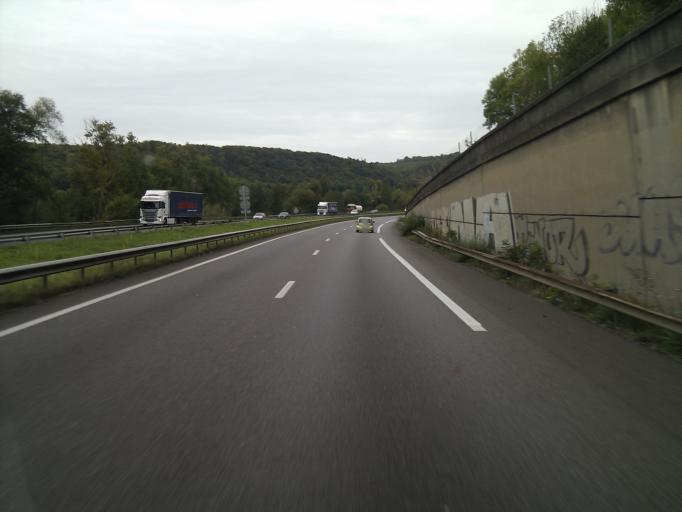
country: FR
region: Lorraine
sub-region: Departement de Meurthe-et-Moselle
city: Custines
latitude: 48.7915
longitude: 6.1293
